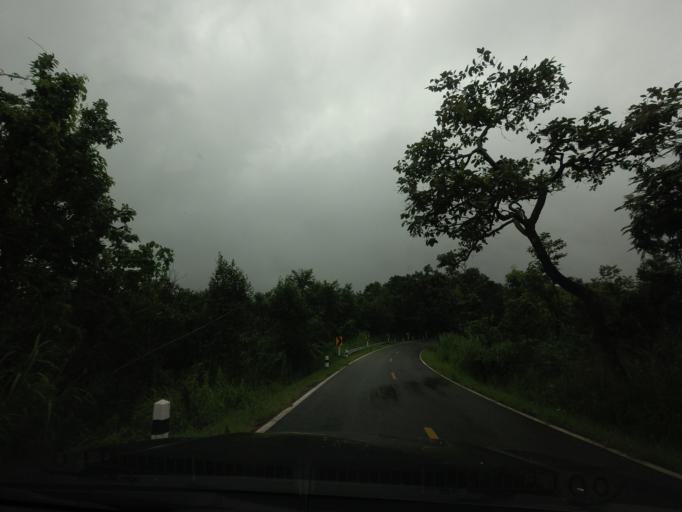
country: TH
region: Nong Khai
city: Sangkhom
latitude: 18.0366
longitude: 102.3339
